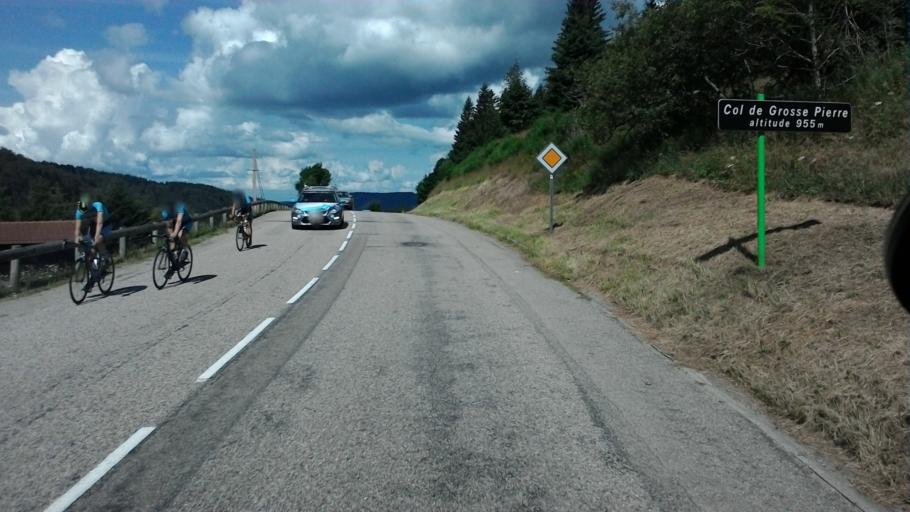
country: FR
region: Lorraine
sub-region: Departement des Vosges
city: La Bresse
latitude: 48.0268
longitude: 6.8844
